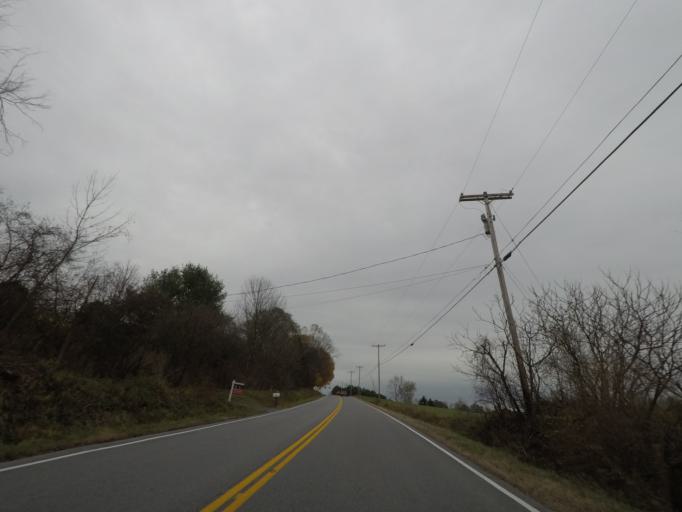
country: US
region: New York
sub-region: Schenectady County
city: East Glenville
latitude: 42.8966
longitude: -73.8736
